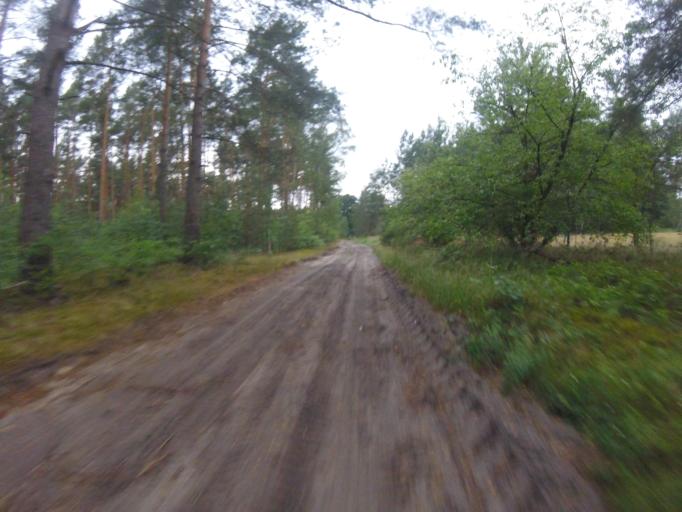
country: DE
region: Brandenburg
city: Gross Koris
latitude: 52.1935
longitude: 13.6415
